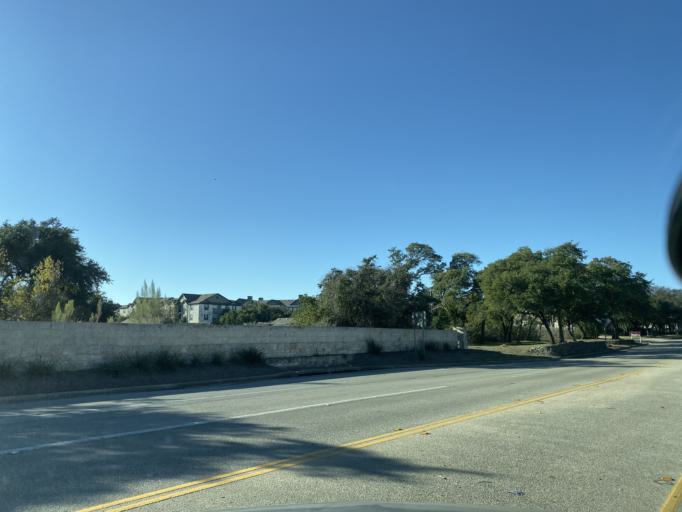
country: US
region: Texas
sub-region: Williamson County
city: Jollyville
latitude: 30.4713
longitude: -97.7633
